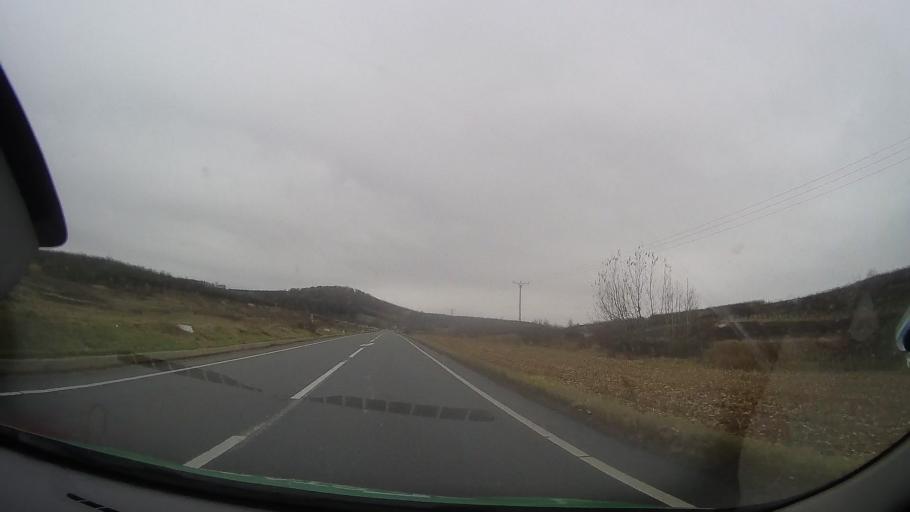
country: RO
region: Mures
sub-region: Comuna Breaza
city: Breaza
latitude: 46.7833
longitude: 24.6520
